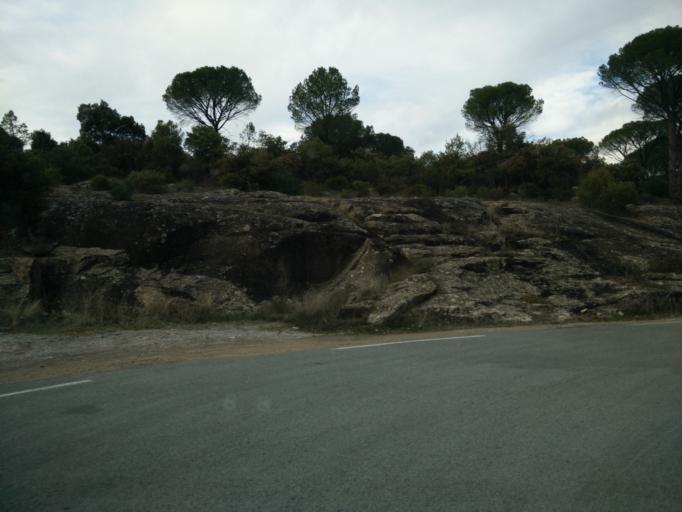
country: FR
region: Provence-Alpes-Cote d'Azur
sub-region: Departement du Var
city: Vidauban
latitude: 43.3974
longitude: 6.4556
